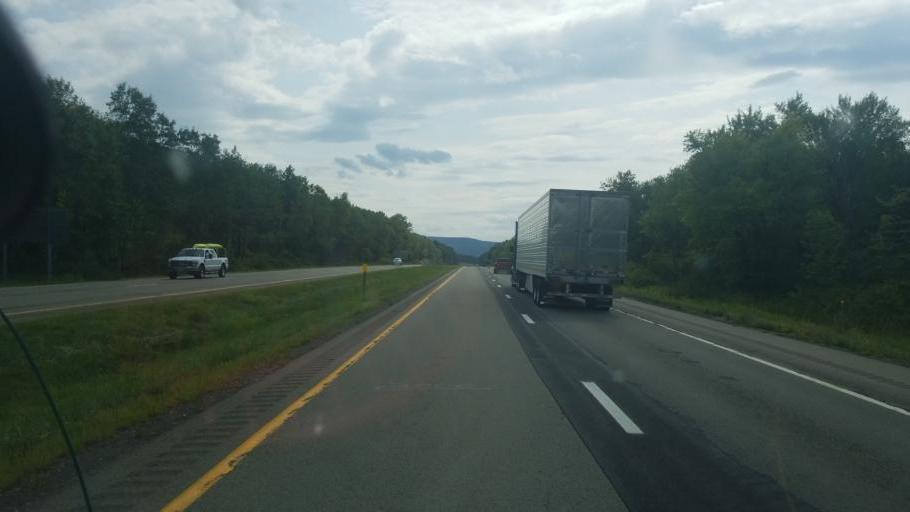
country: US
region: New York
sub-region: Cattaraugus County
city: Salamanca
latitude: 42.1470
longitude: -78.7674
